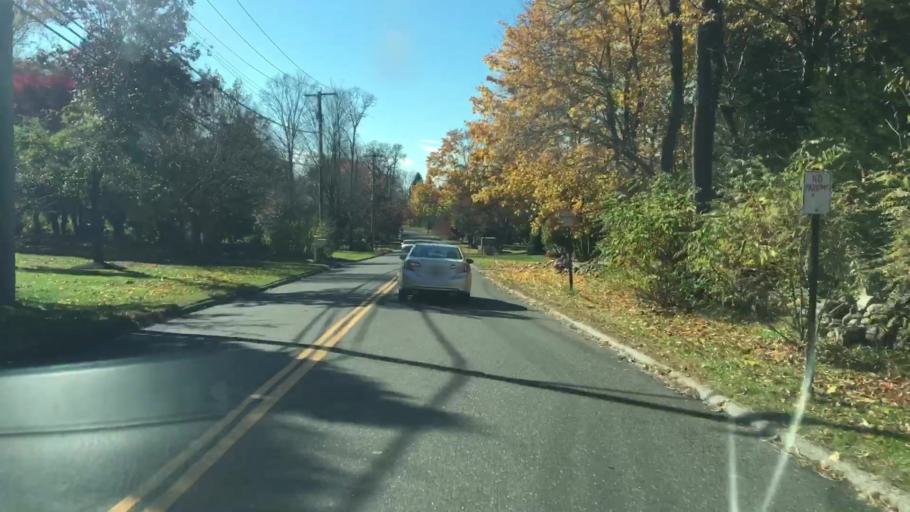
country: US
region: Connecticut
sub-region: Fairfield County
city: Trumbull
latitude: 41.2404
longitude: -73.1685
